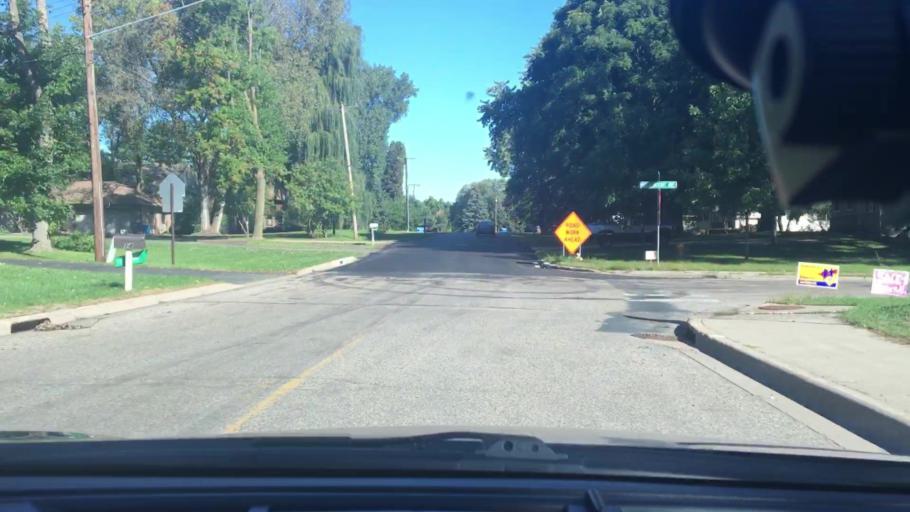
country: US
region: Minnesota
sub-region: Hennepin County
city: Plymouth
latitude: 44.9785
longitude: -93.4476
